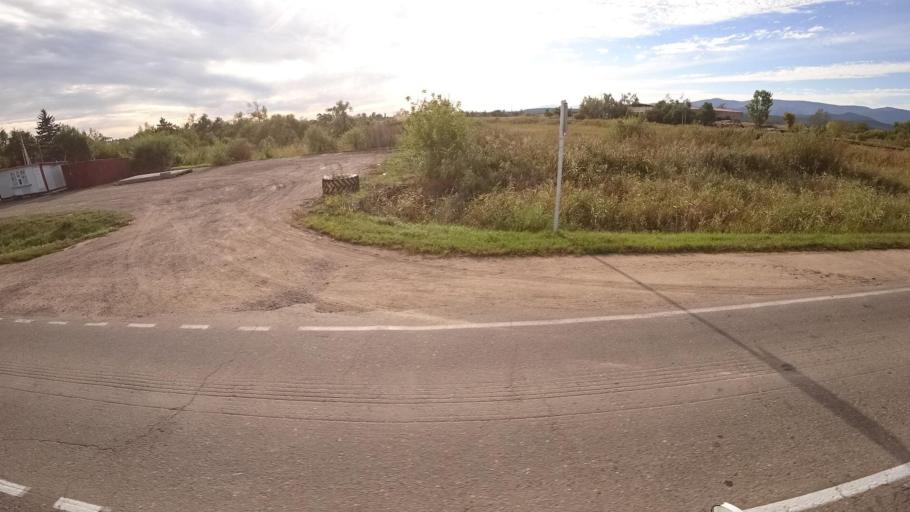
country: RU
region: Primorskiy
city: Dostoyevka
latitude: 44.2959
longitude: 133.4265
